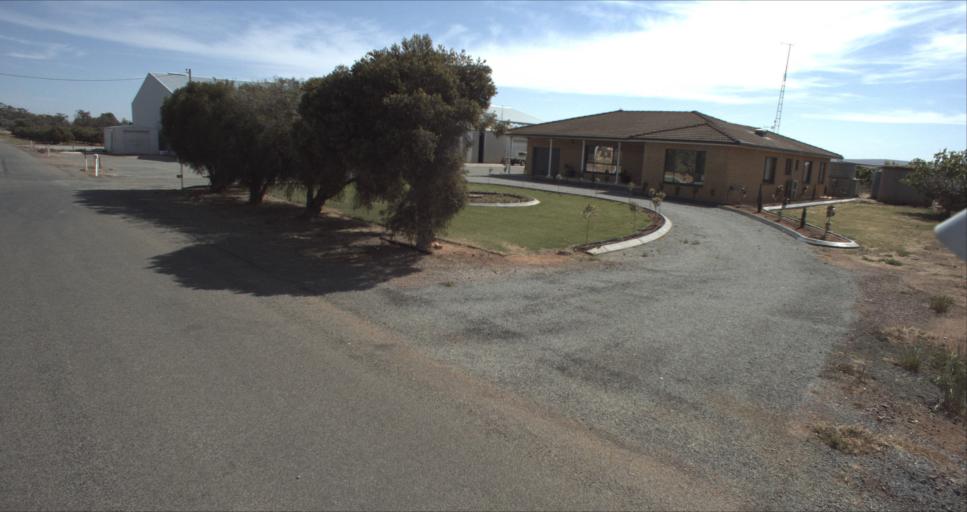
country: AU
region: New South Wales
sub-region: Leeton
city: Leeton
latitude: -34.5804
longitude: 146.4690
